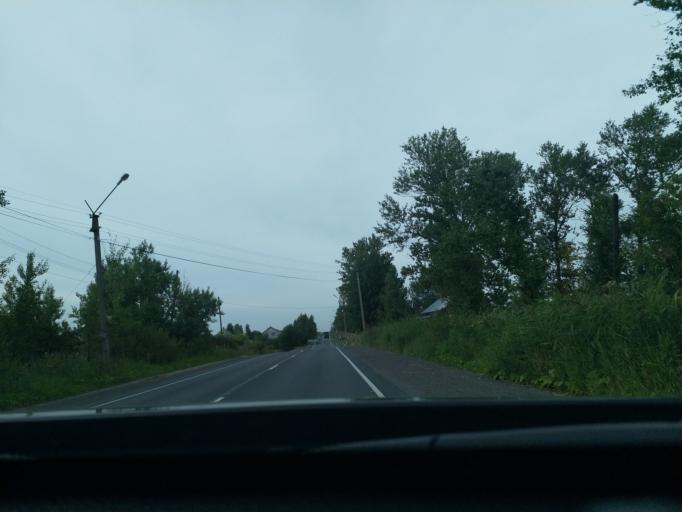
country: RU
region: Leningrad
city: Nikol'skoye
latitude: 59.7129
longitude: 30.7796
